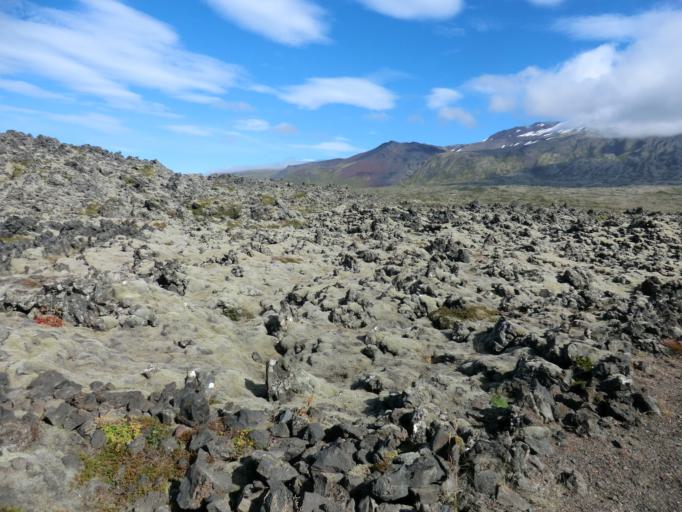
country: IS
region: West
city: Olafsvik
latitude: 64.7587
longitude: -23.8840
